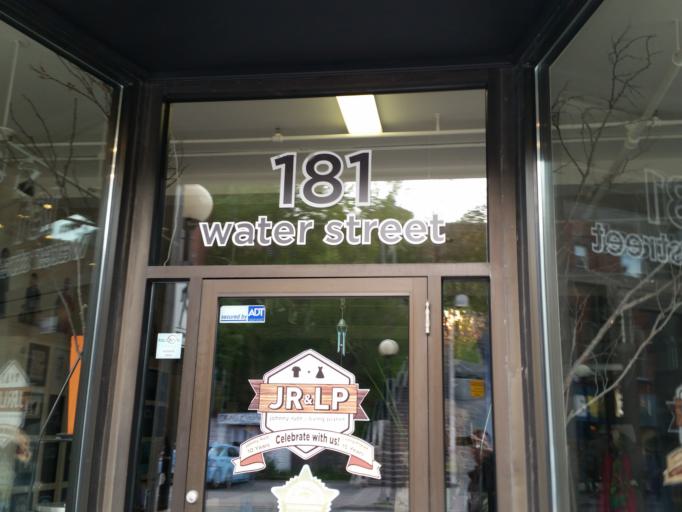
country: CA
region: Newfoundland and Labrador
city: St. John's
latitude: 47.5644
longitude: -52.7067
